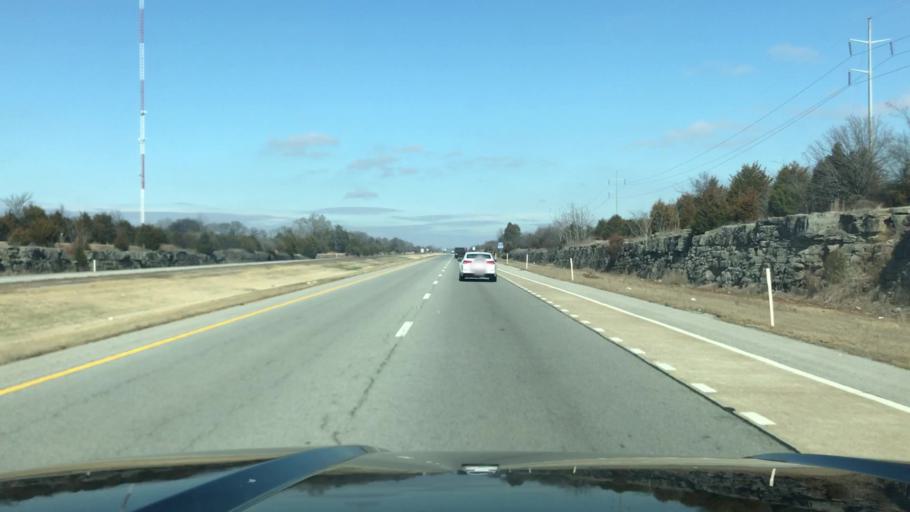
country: US
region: Tennessee
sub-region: Wilson County
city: Rural Hill
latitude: 36.0766
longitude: -86.4289
